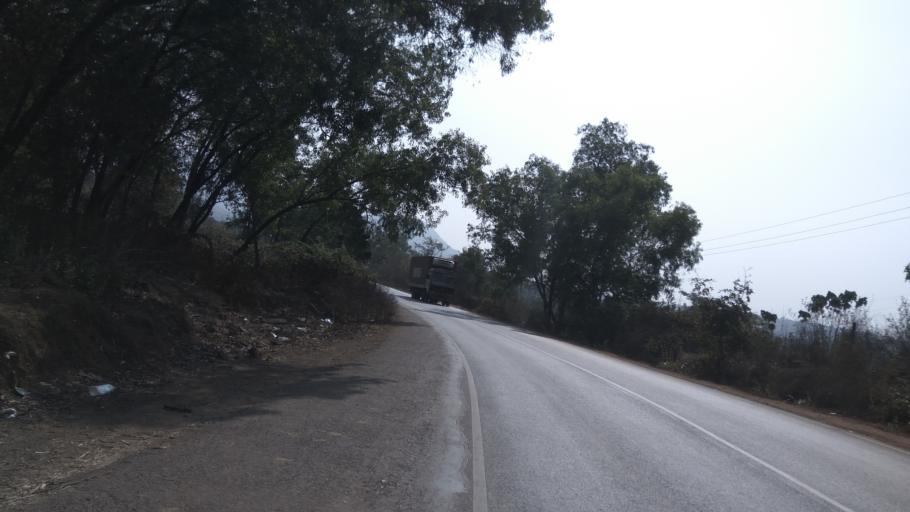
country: IN
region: Goa
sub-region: North Goa
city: Palle
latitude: 15.4153
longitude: 74.0766
